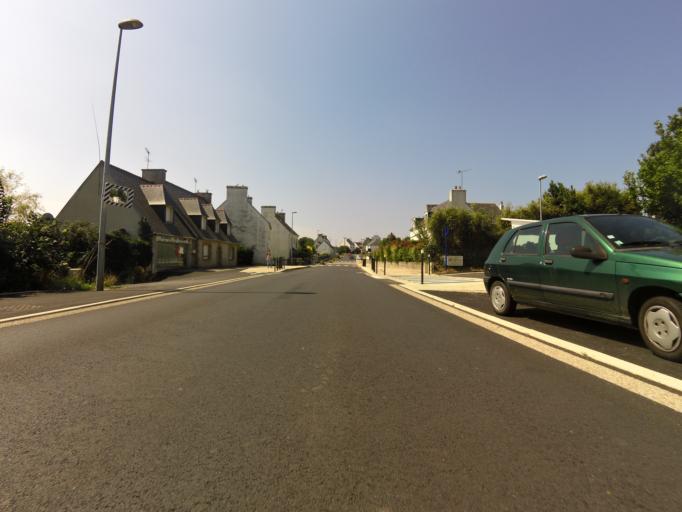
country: FR
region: Brittany
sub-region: Departement du Finistere
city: Ploneour-Lanvern
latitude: 47.9065
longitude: -4.2728
